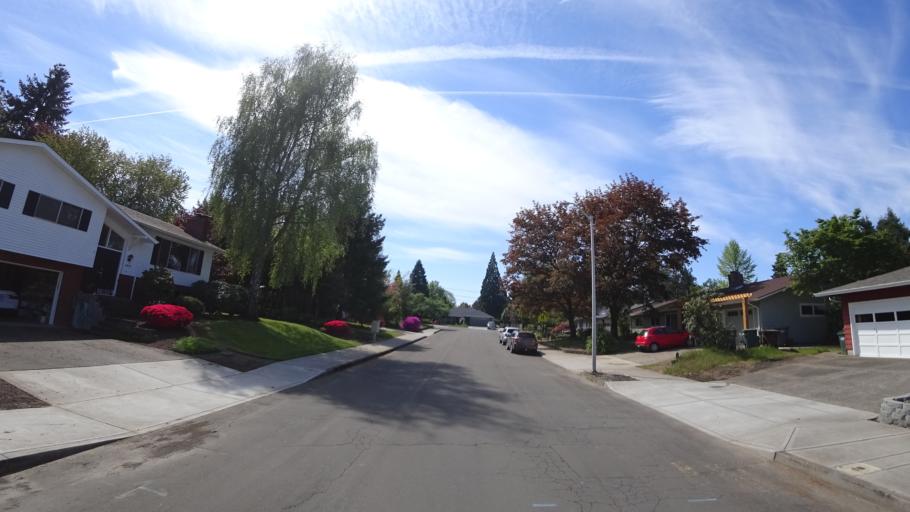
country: US
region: Oregon
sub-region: Washington County
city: Hillsboro
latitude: 45.5135
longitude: -122.9573
